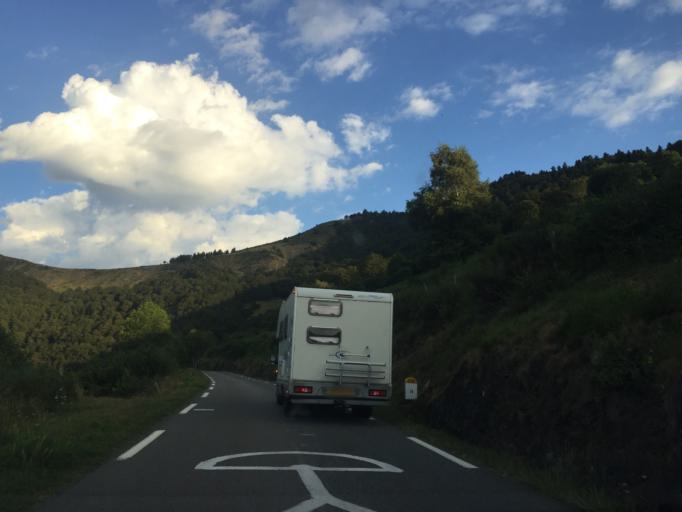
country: FR
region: Midi-Pyrenees
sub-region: Departement des Hautes-Pyrenees
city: Saint-Lary-Soulan
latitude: 42.9388
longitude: 0.3391
